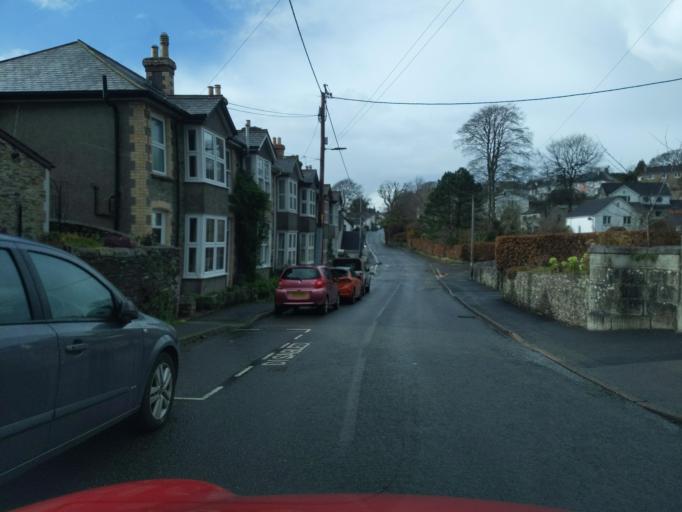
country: GB
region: England
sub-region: Devon
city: Tavistock
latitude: 50.5359
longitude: -4.1350
